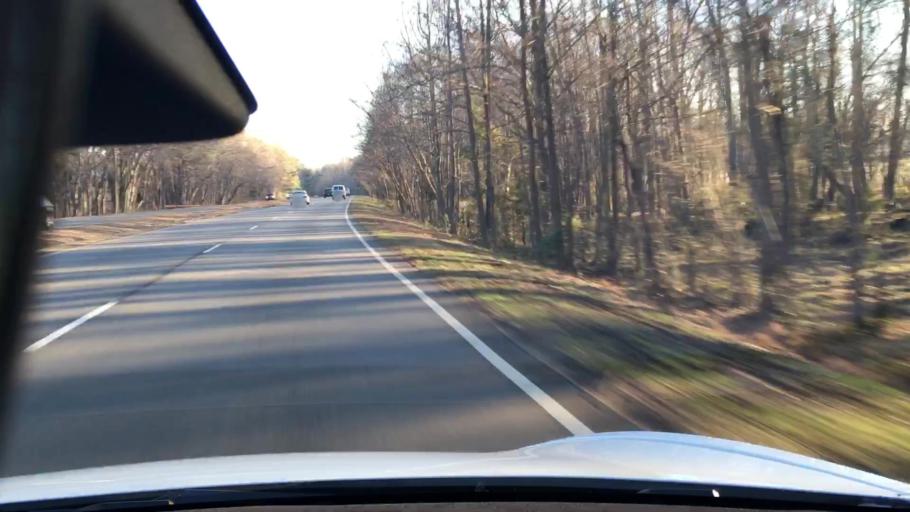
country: US
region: Virginia
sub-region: Henrico County
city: Fort Lee
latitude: 37.4691
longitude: -77.3777
